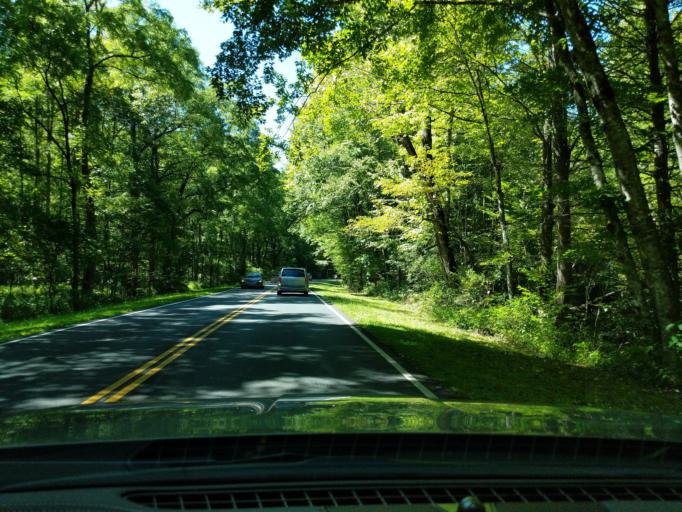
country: US
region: North Carolina
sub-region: Swain County
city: Cherokee
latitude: 35.5573
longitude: -83.3201
